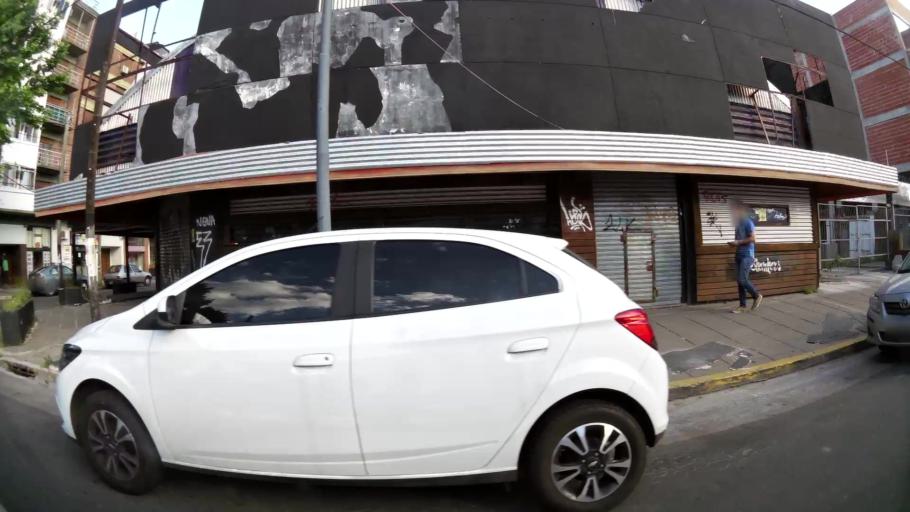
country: AR
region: Buenos Aires
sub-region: Partido de General San Martin
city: General San Martin
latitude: -34.5460
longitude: -58.5499
